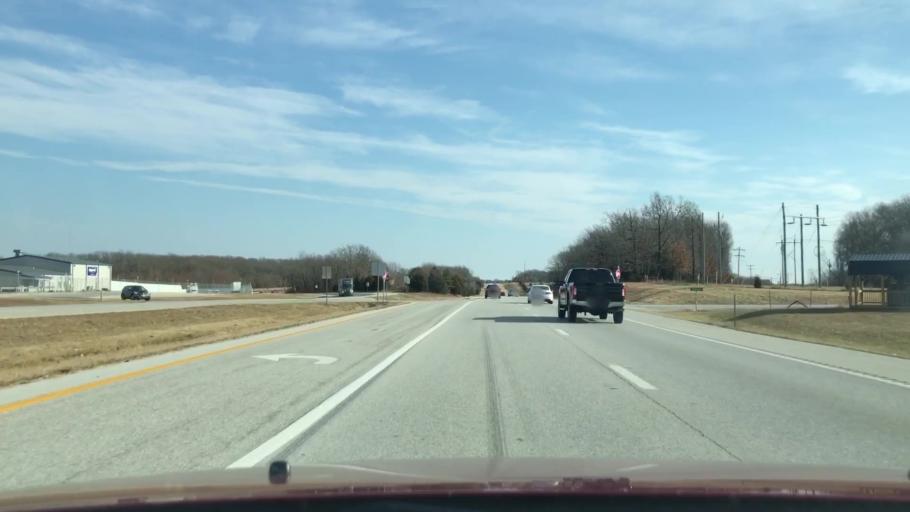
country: US
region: Missouri
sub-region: Webster County
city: Rogersville
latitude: 37.1186
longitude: -93.0147
